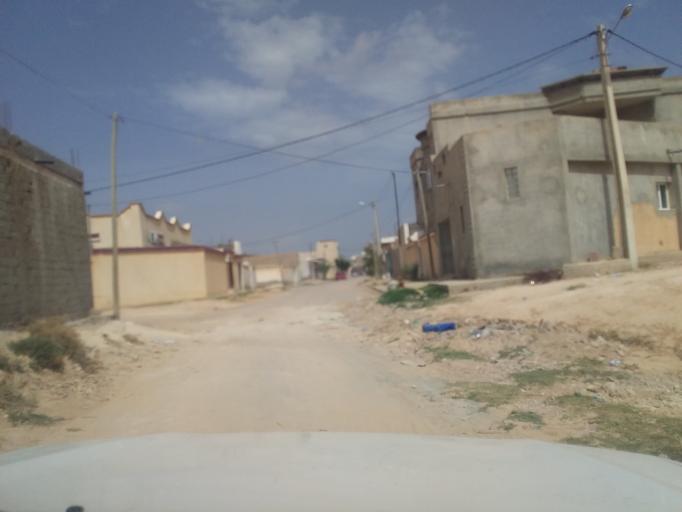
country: TN
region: Qabis
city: Matmata
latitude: 33.6149
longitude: 10.2793
